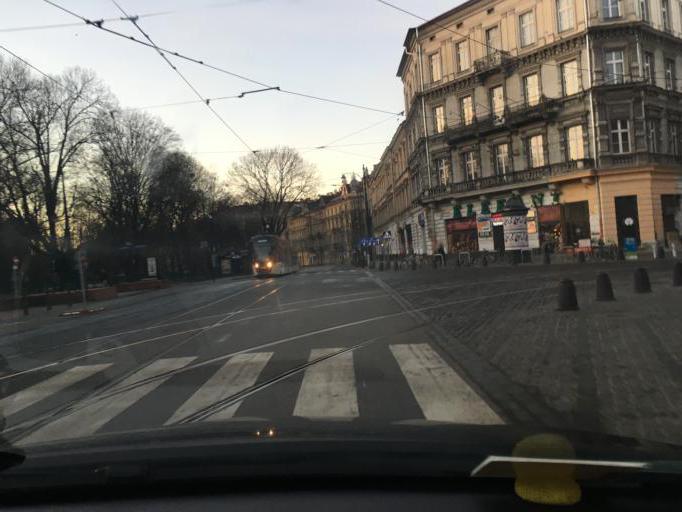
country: PL
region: Lesser Poland Voivodeship
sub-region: Krakow
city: Krakow
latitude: 50.0636
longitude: 19.9331
